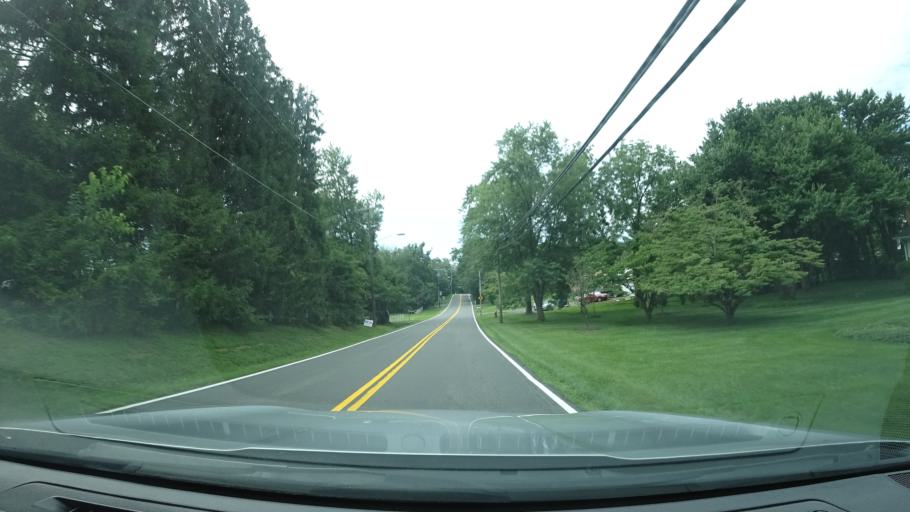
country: US
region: Virginia
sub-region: Fairfax County
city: Great Falls
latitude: 38.9906
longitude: -77.2877
